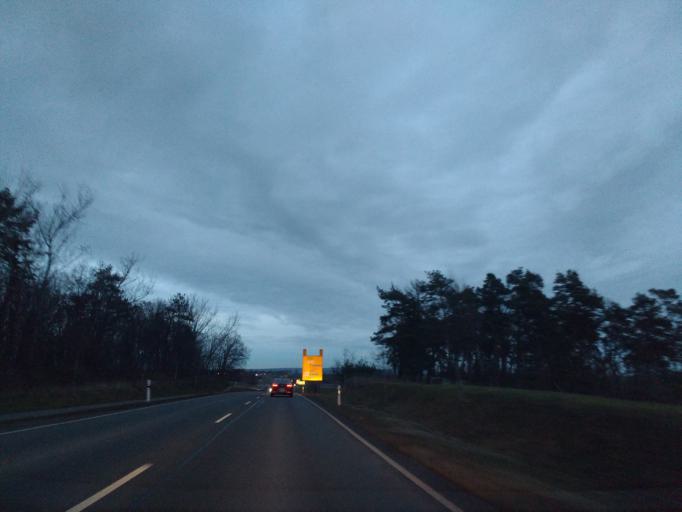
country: DE
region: Saxony-Anhalt
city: Ditfurt
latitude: 51.8024
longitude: 11.1907
